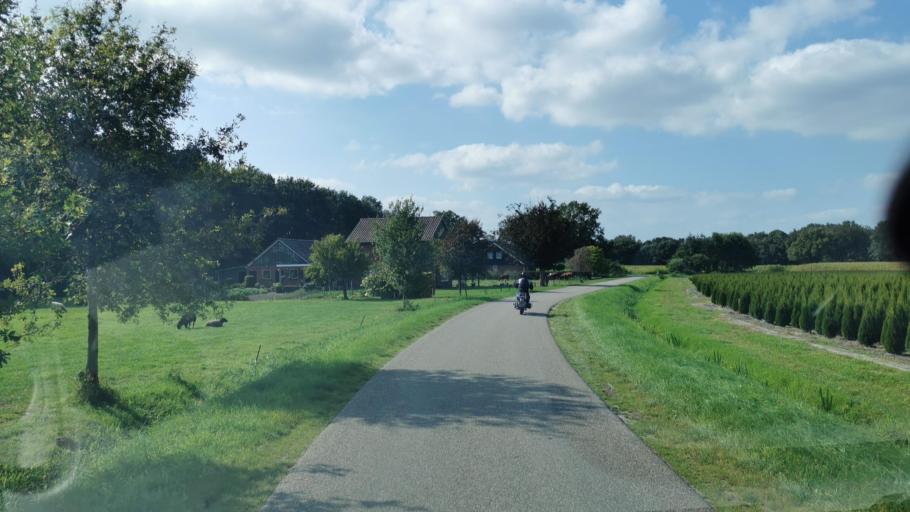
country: NL
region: Overijssel
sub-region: Gemeente Hengelo
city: Hengelo
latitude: 52.3225
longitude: 6.8026
